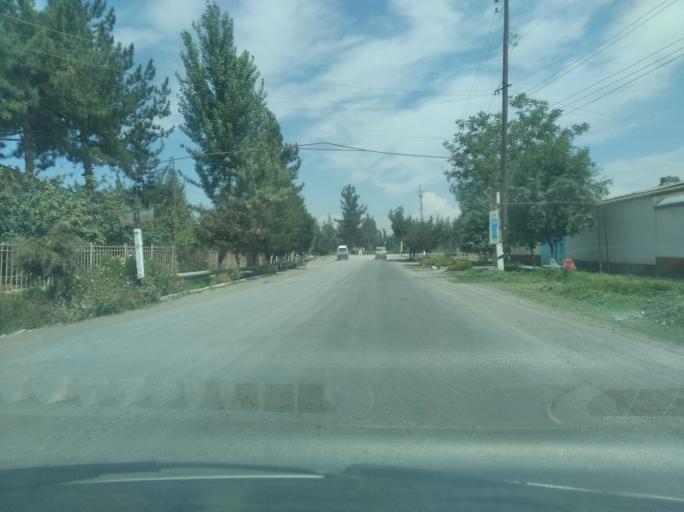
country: UZ
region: Andijon
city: Khujaobod
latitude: 40.6375
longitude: 72.4494
